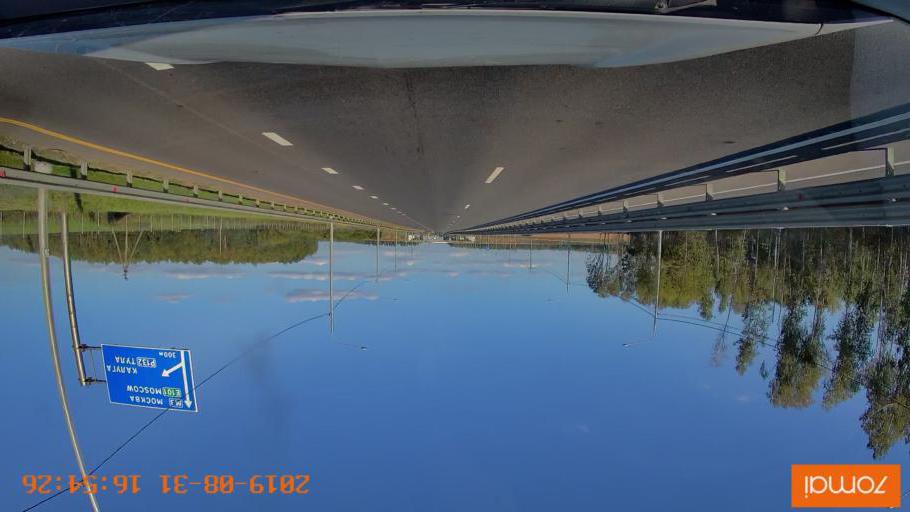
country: RU
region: Kaluga
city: Detchino
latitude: 54.7702
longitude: 36.2326
